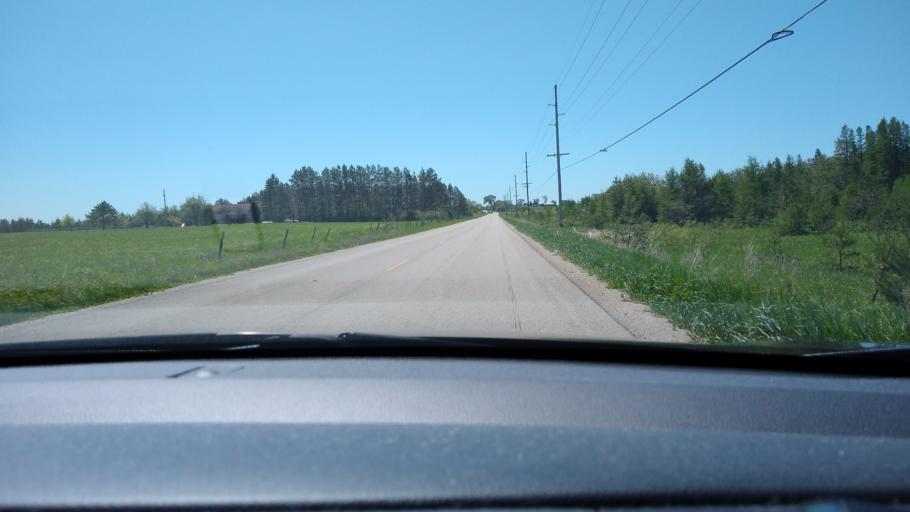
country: US
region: Michigan
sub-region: Delta County
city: Escanaba
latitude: 45.8476
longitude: -87.1841
